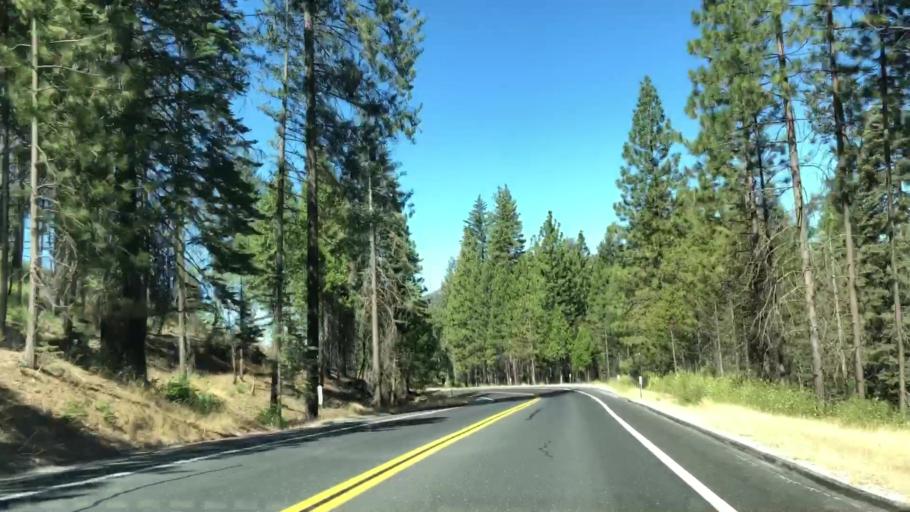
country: US
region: California
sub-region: Mariposa County
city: Midpines
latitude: 37.8138
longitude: -119.8967
